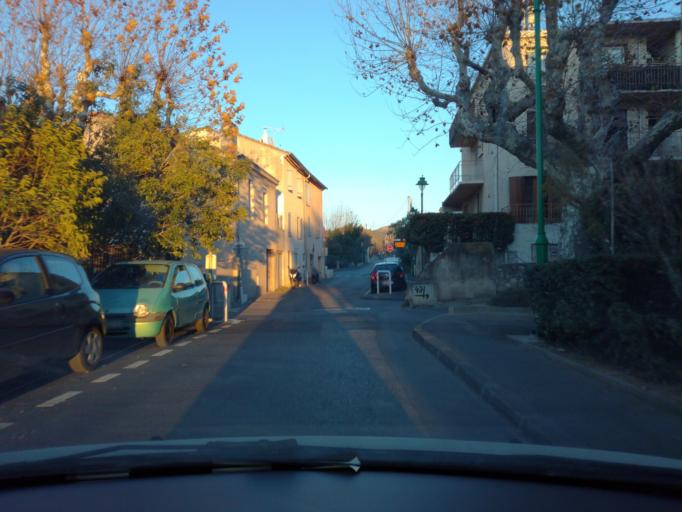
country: FR
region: Provence-Alpes-Cote d'Azur
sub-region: Departement des Bouches-du-Rhone
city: Plan-de-Cuques
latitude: 43.3324
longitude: 5.4631
